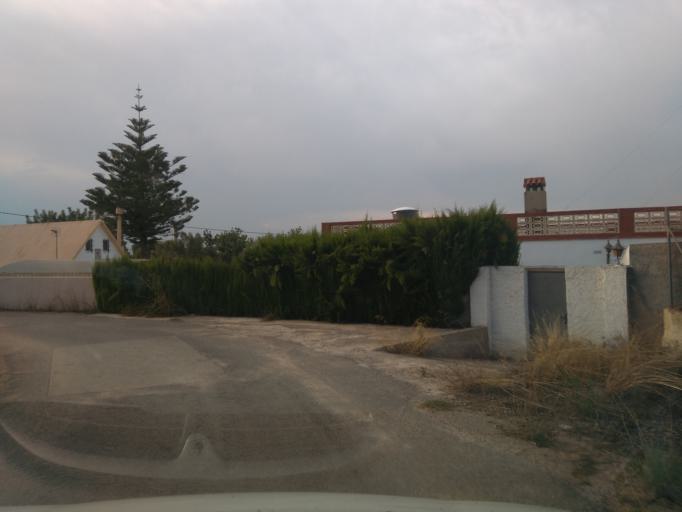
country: ES
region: Valencia
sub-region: Provincia de Valencia
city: Ribarroja
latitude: 39.5458
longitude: -0.5857
